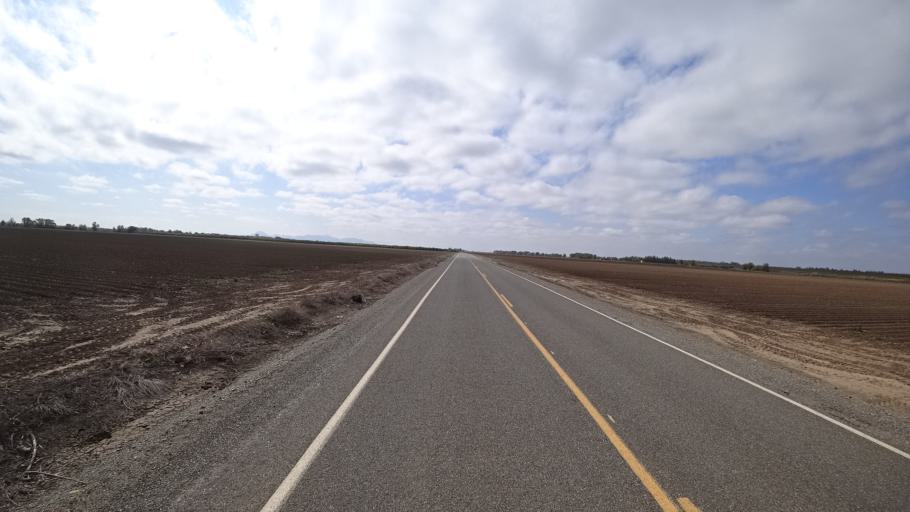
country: US
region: California
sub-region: Butte County
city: Biggs
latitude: 39.4194
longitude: -121.9295
